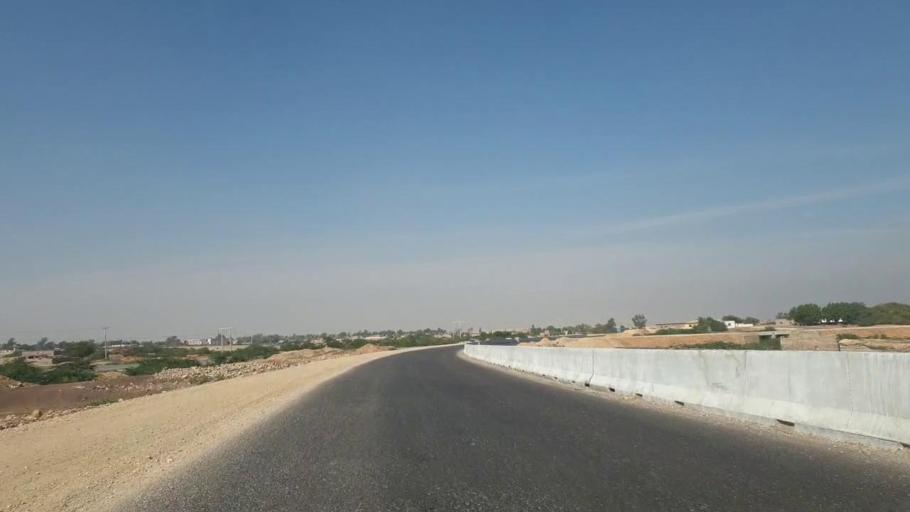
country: PK
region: Sindh
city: Matiari
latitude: 25.6603
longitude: 68.2964
